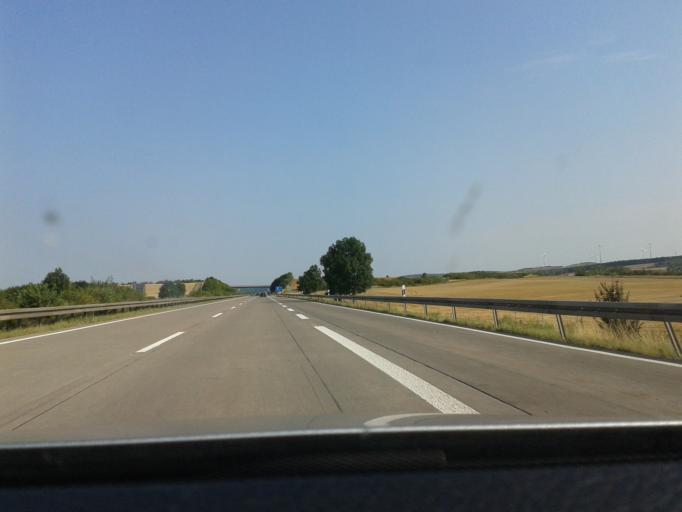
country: DE
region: Thuringia
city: Nordhausen
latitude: 51.4704
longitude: 10.7825
